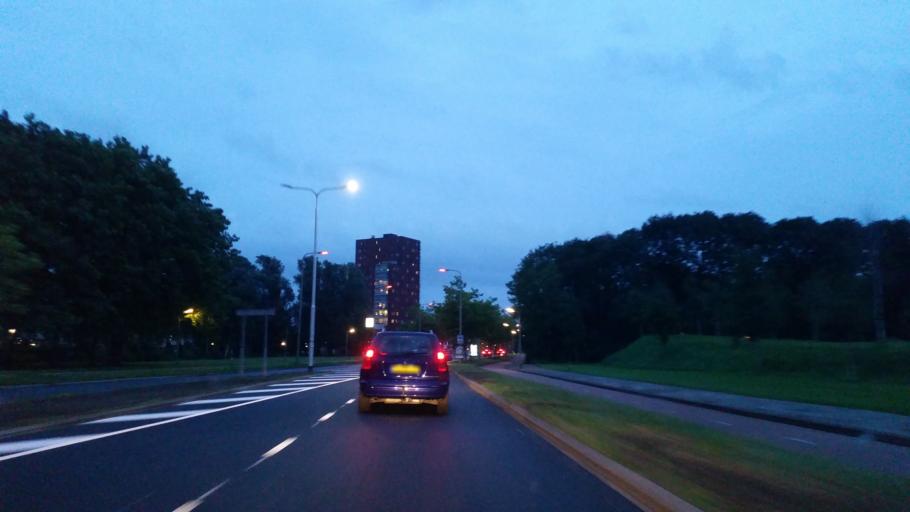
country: NL
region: Friesland
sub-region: Gemeente Leeuwarden
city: Bilgaard
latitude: 53.2131
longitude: 5.7994
